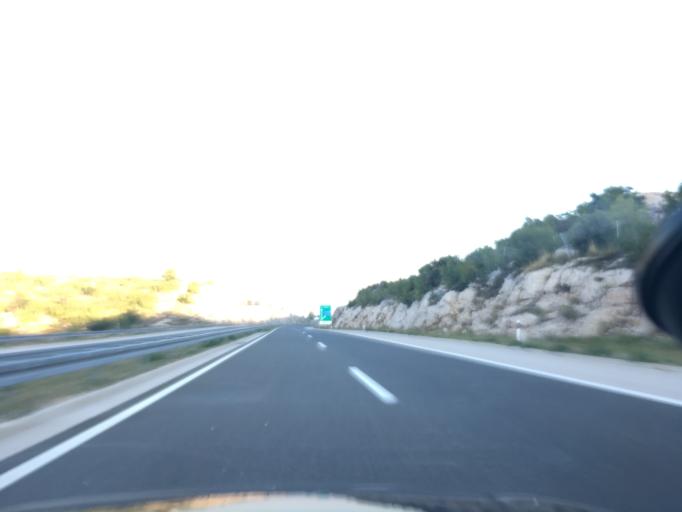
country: HR
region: Sibensko-Kniniska
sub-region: Grad Sibenik
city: Sibenik
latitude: 43.7588
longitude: 15.9393
